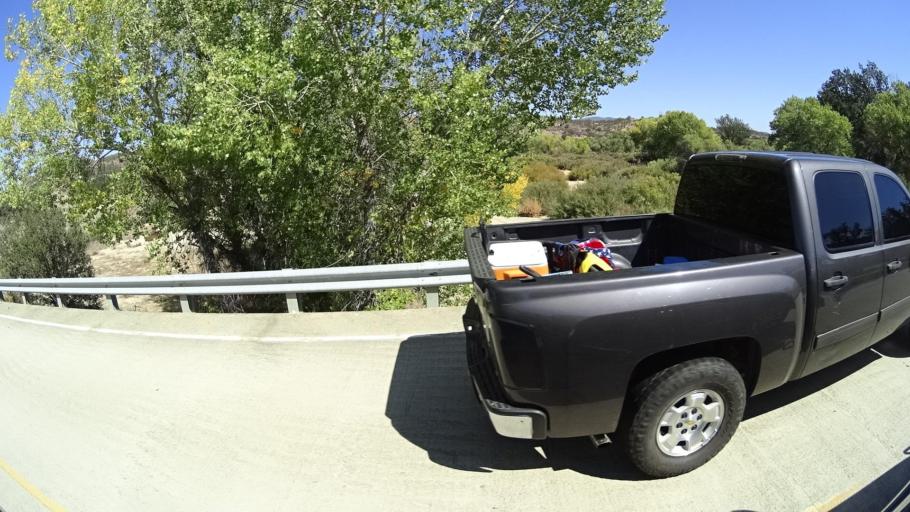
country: US
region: California
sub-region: San Luis Obispo County
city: Lake Nacimiento
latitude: 35.8964
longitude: -121.0892
